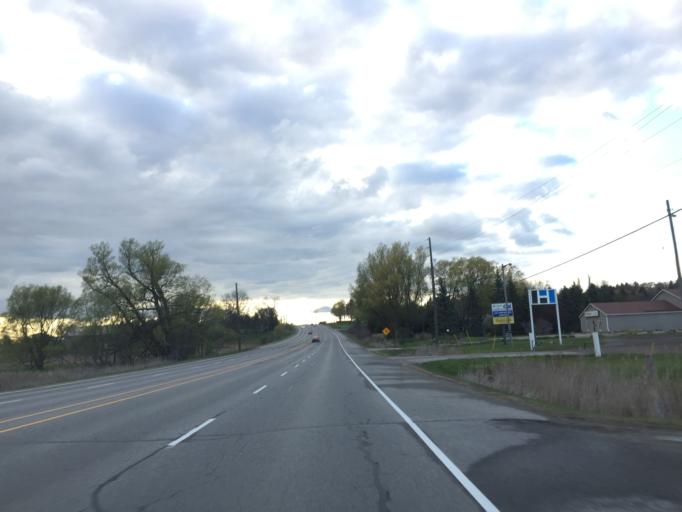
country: CA
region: Ontario
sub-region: Wellington County
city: Guelph
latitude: 43.5775
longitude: -80.2871
